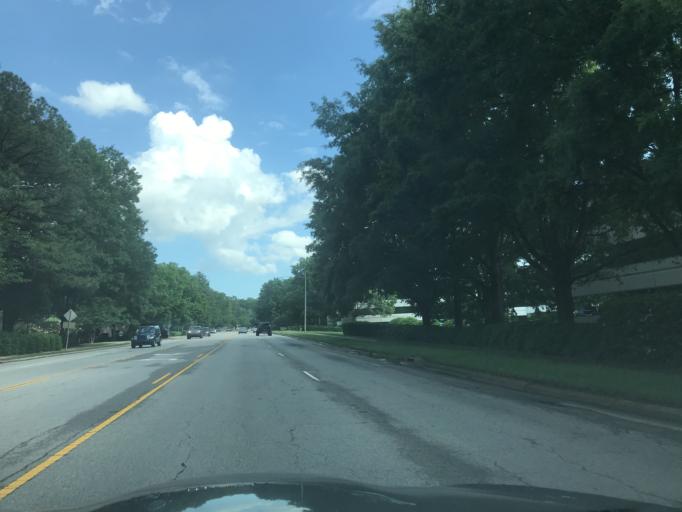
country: US
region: North Carolina
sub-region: Wake County
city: West Raleigh
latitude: 35.8709
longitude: -78.6412
